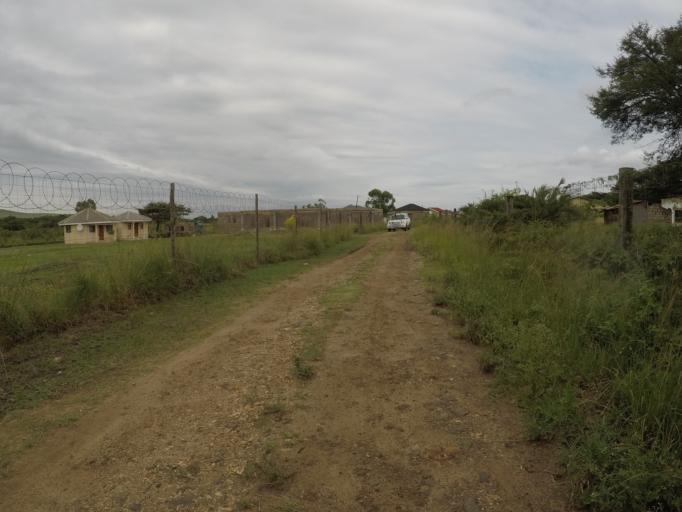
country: ZA
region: KwaZulu-Natal
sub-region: uThungulu District Municipality
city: Empangeni
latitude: -28.7151
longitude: 31.8647
